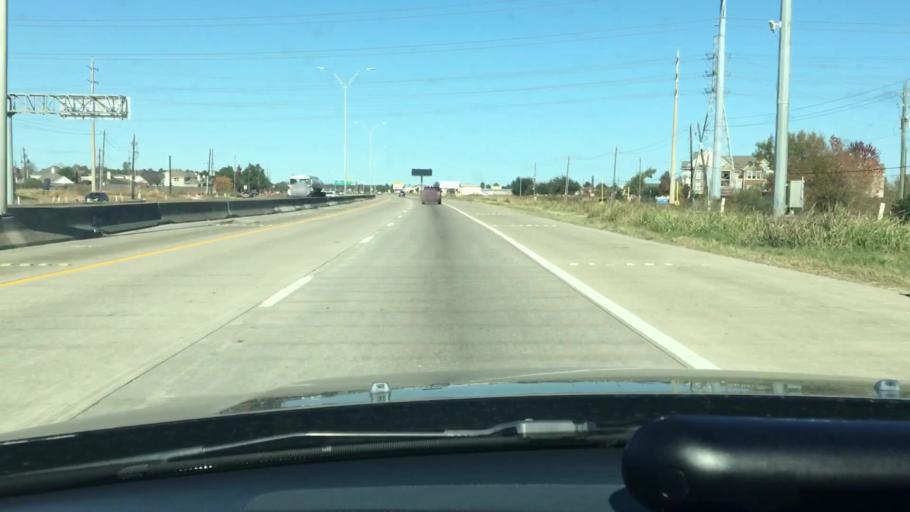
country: US
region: Texas
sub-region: Harris County
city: Cloverleaf
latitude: 29.8164
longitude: -95.1644
